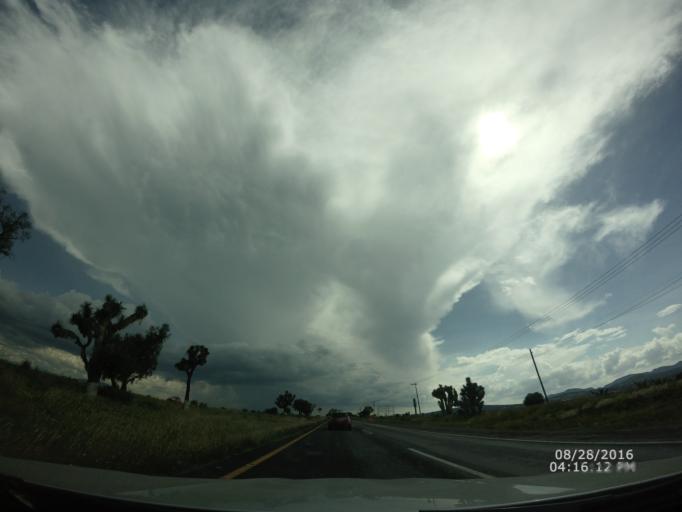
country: MX
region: Hidalgo
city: Zapotlan de Juarez
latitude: 19.9894
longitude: -98.8404
